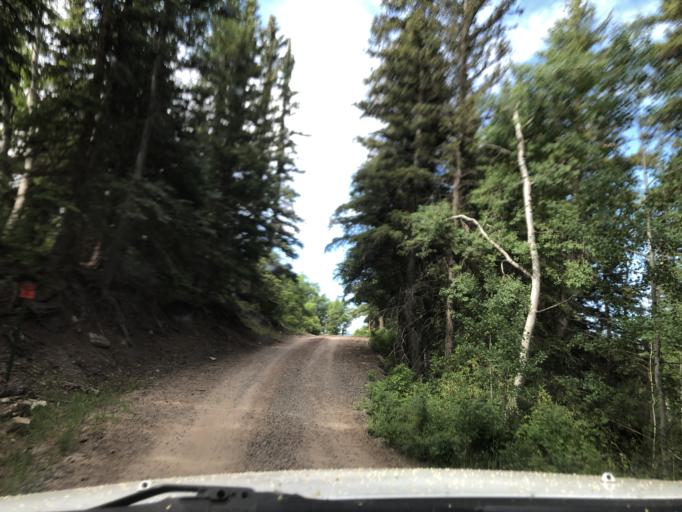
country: US
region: Colorado
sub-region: Delta County
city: Paonia
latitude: 39.0266
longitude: -107.3434
